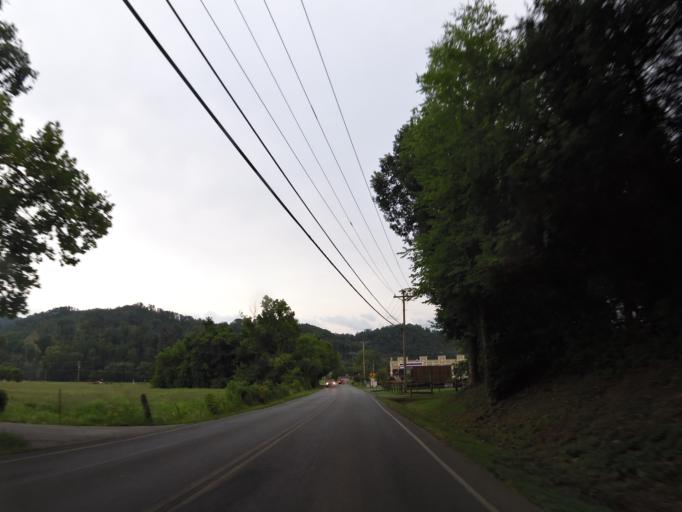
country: US
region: Tennessee
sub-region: Sevier County
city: Pigeon Forge
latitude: 35.7894
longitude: -83.6268
